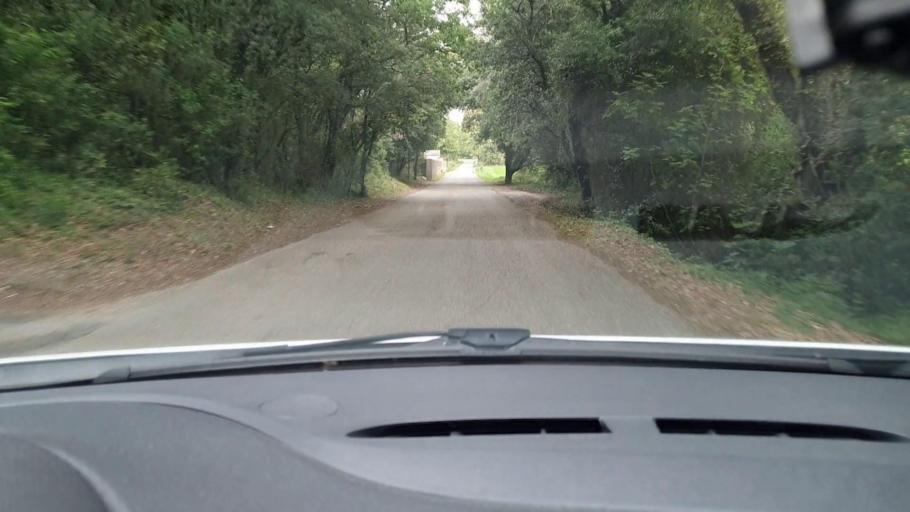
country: FR
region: Languedoc-Roussillon
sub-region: Departement du Gard
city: Montaren-et-Saint-Mediers
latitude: 44.0532
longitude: 4.3233
